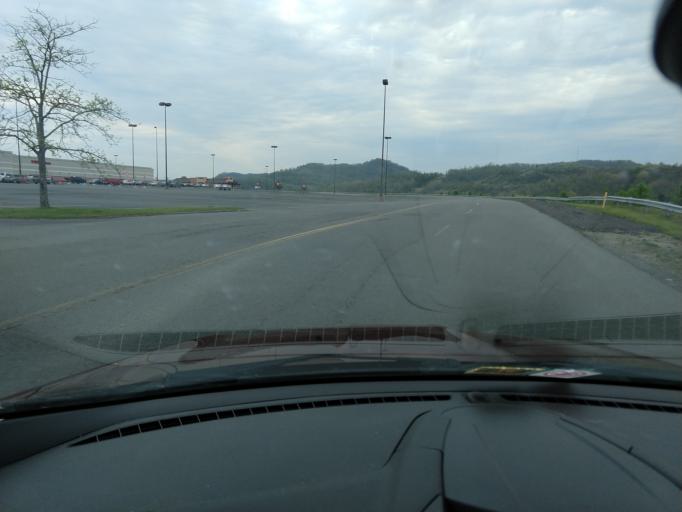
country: US
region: West Virginia
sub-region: Harrison County
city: Bridgeport
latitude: 39.3129
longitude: -80.2749
